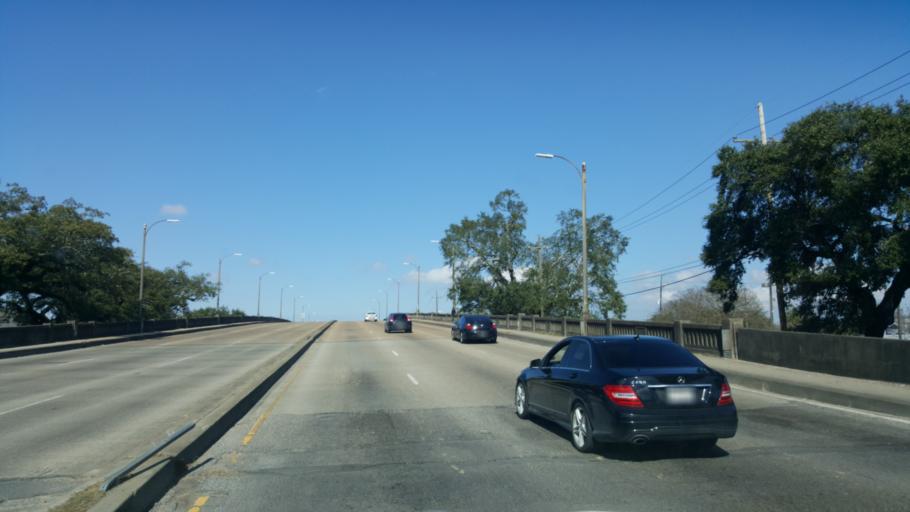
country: US
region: Louisiana
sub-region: Orleans Parish
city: New Orleans
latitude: 29.9836
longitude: -90.0580
